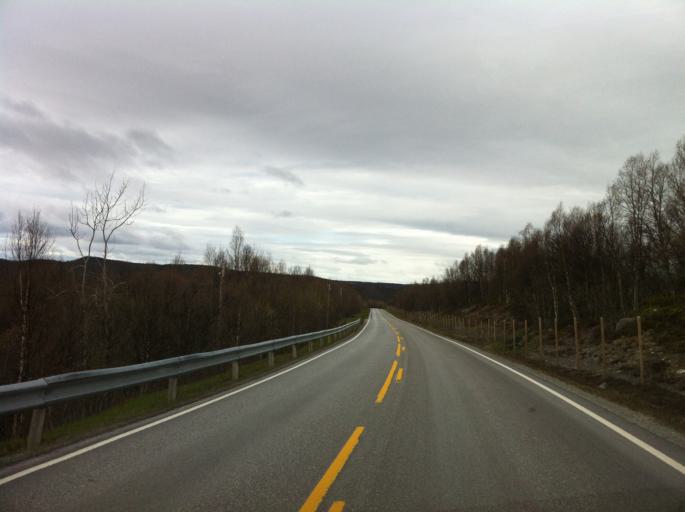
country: NO
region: Sor-Trondelag
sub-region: Tydal
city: Aas
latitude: 62.6377
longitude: 11.9091
